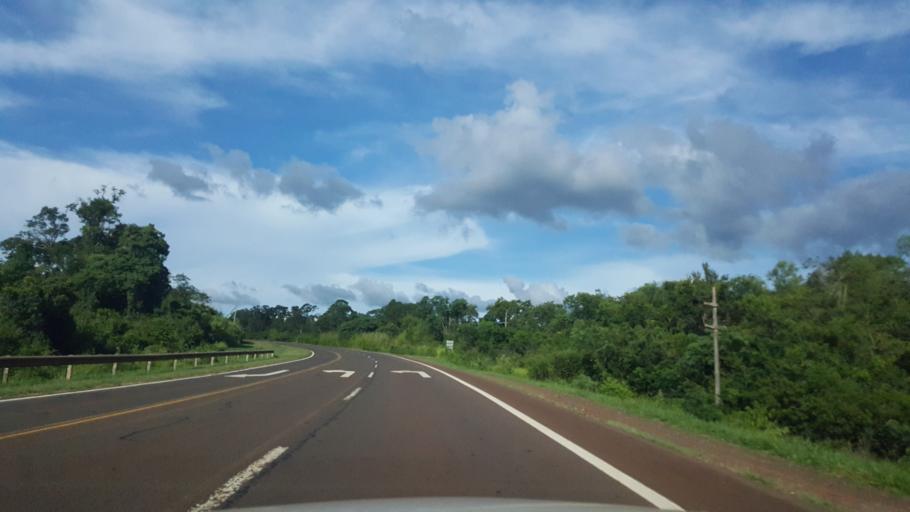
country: AR
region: Misiones
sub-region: Departamento de Candelaria
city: Loreto
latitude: -27.3532
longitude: -55.5509
